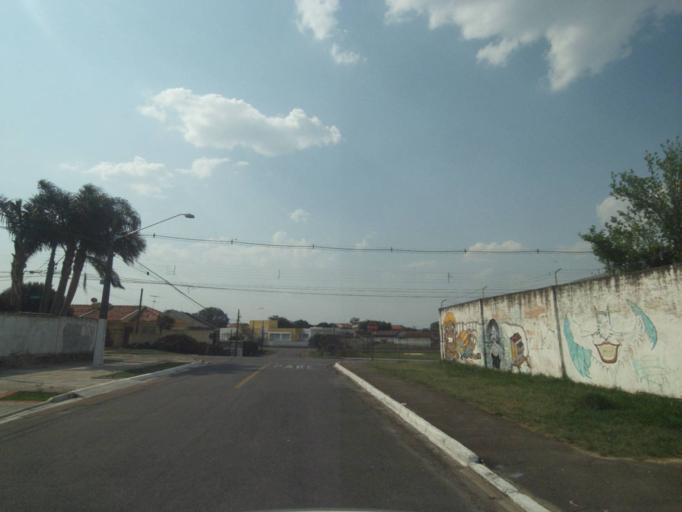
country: BR
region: Parana
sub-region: Sao Jose Dos Pinhais
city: Sao Jose dos Pinhais
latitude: -25.5356
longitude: -49.2397
